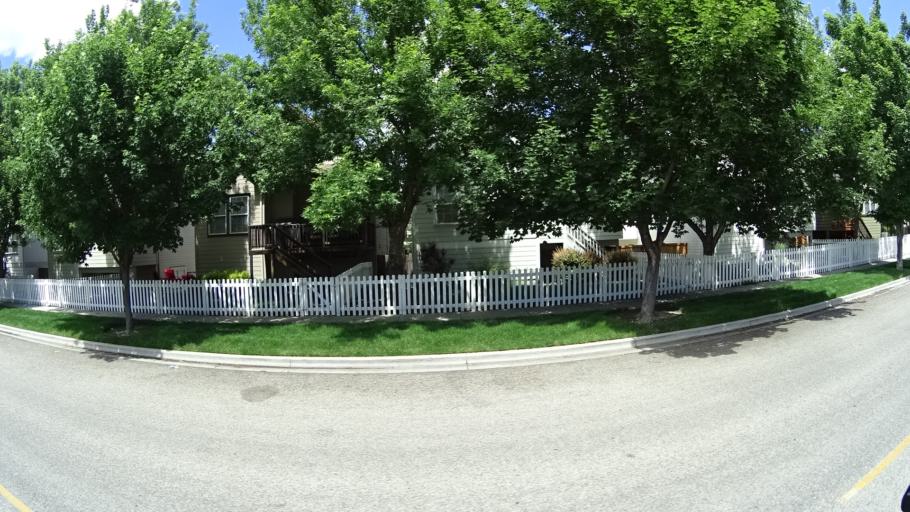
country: US
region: Idaho
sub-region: Ada County
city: Boise
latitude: 43.5946
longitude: -116.1853
